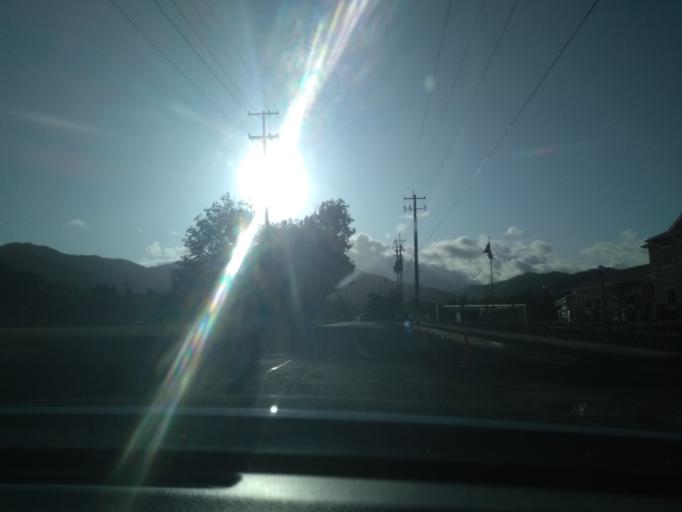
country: US
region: California
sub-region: Mendocino County
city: Ukiah
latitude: 39.1594
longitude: -123.2018
